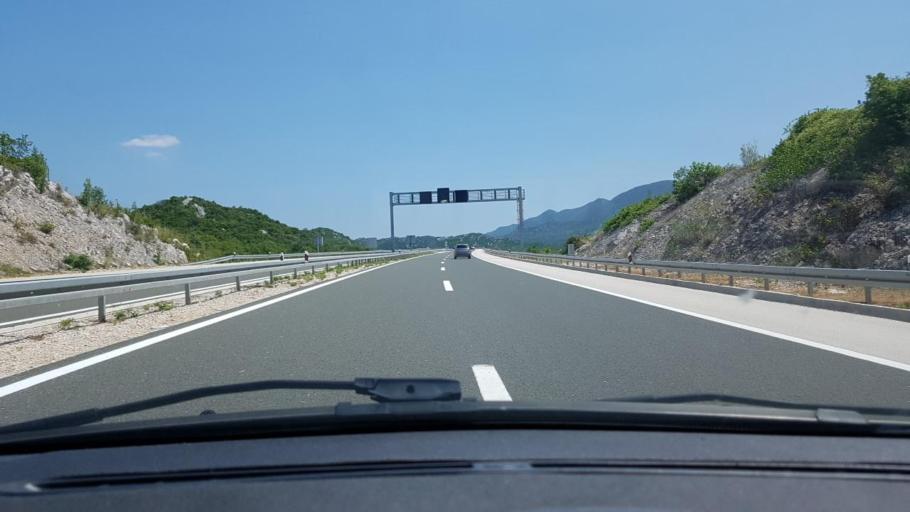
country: HR
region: Splitsko-Dalmatinska
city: Vrgorac
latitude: 43.2092
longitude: 17.2785
